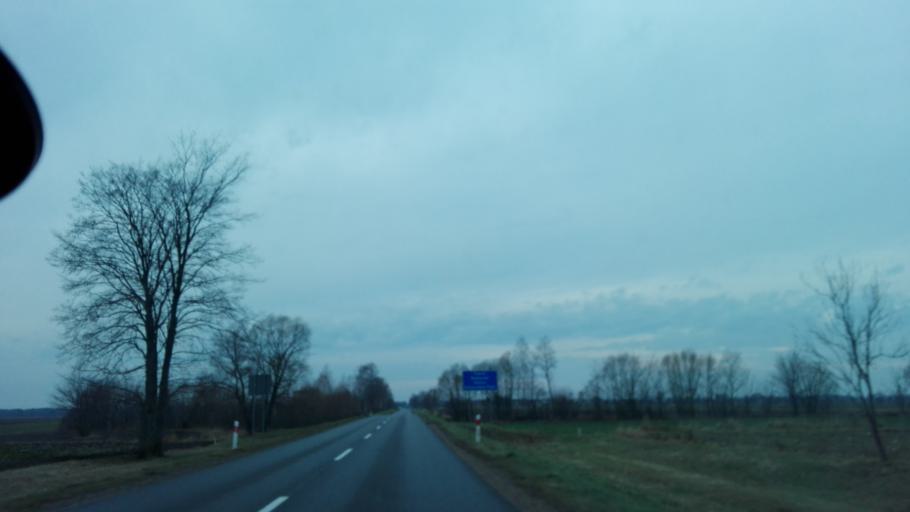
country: PL
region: Lublin Voivodeship
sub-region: Powiat radzynski
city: Komarowka Podlaska
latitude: 51.7761
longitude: 22.9386
